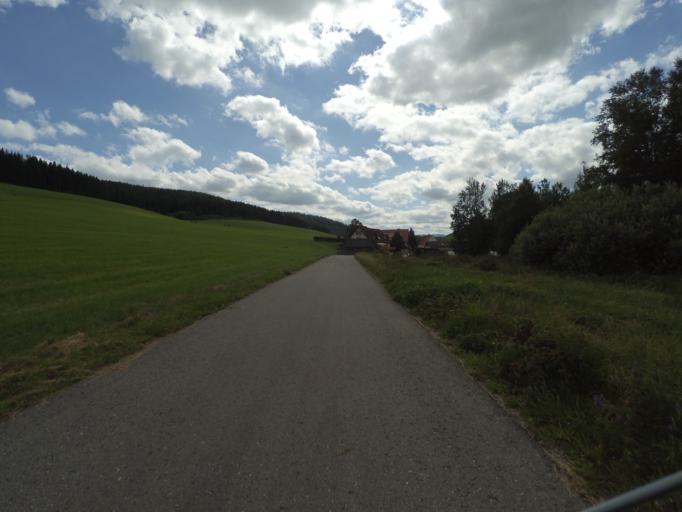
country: DE
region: Baden-Wuerttemberg
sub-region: Freiburg Region
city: Titisee-Neustadt
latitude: 47.9387
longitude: 8.2019
